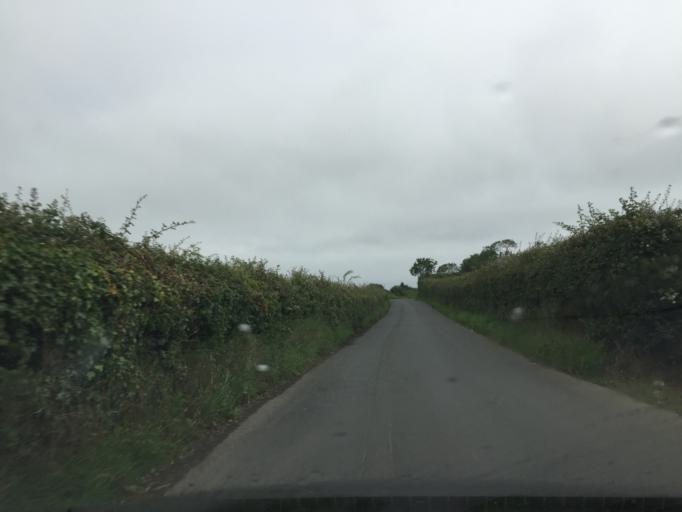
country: GB
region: Northern Ireland
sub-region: Down District
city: Kircubbin
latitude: 54.4907
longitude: -5.5149
